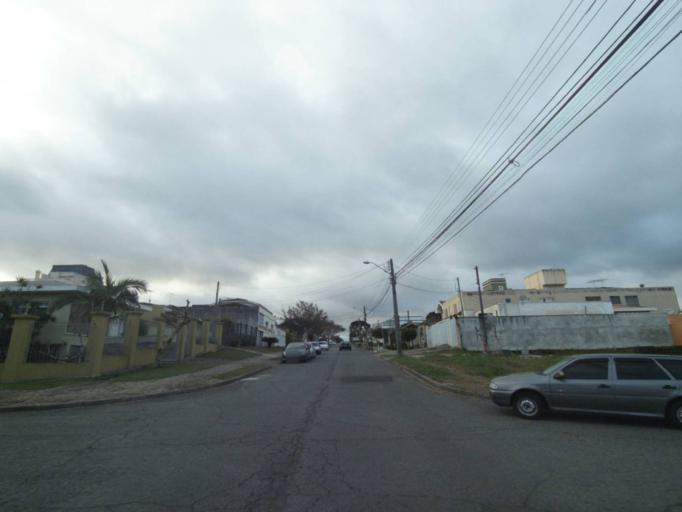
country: BR
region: Parana
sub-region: Curitiba
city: Curitiba
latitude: -25.4572
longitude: -49.2625
